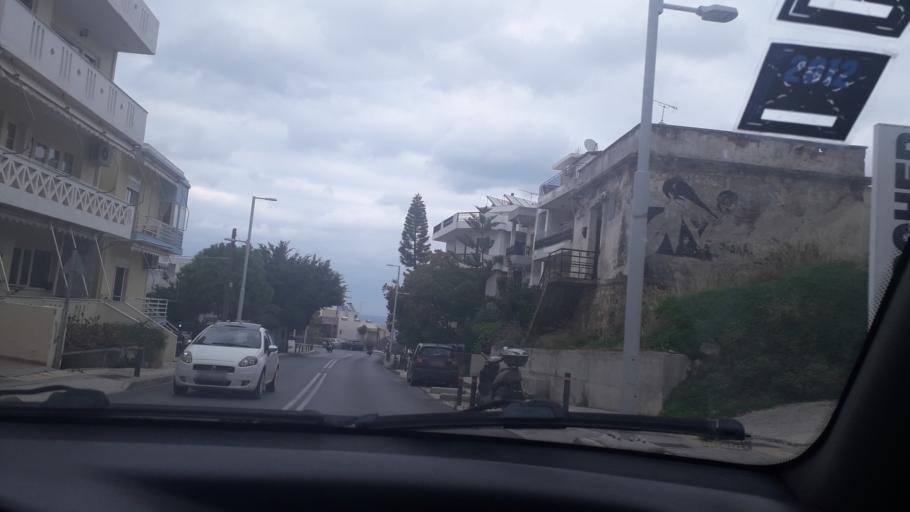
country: GR
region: Crete
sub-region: Nomos Rethymnis
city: Rethymno
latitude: 35.3586
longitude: 24.4762
